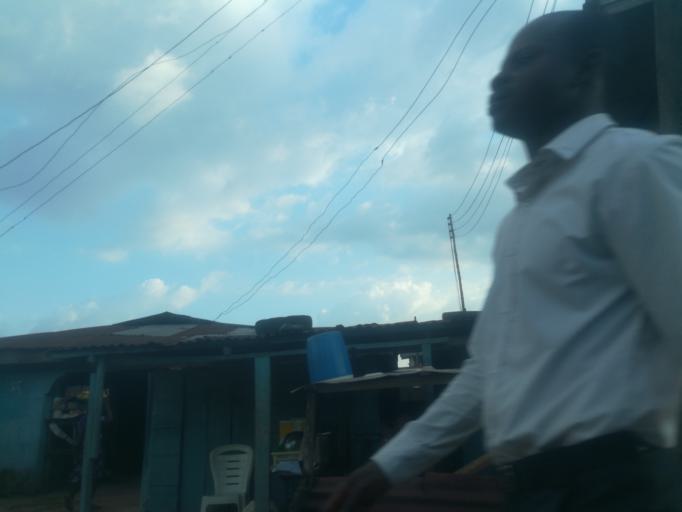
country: NG
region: Oyo
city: Ibadan
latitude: 7.4079
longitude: 3.9482
